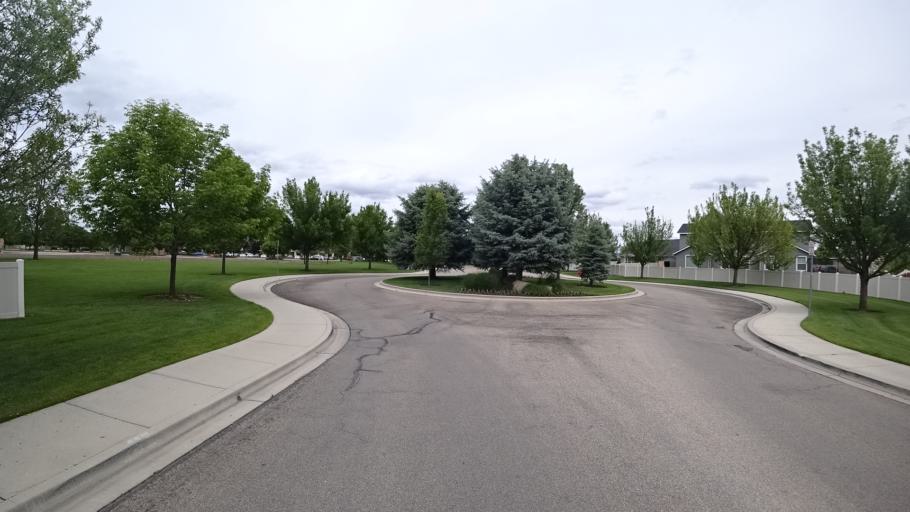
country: US
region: Idaho
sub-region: Ada County
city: Meridian
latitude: 43.6463
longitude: -116.4017
